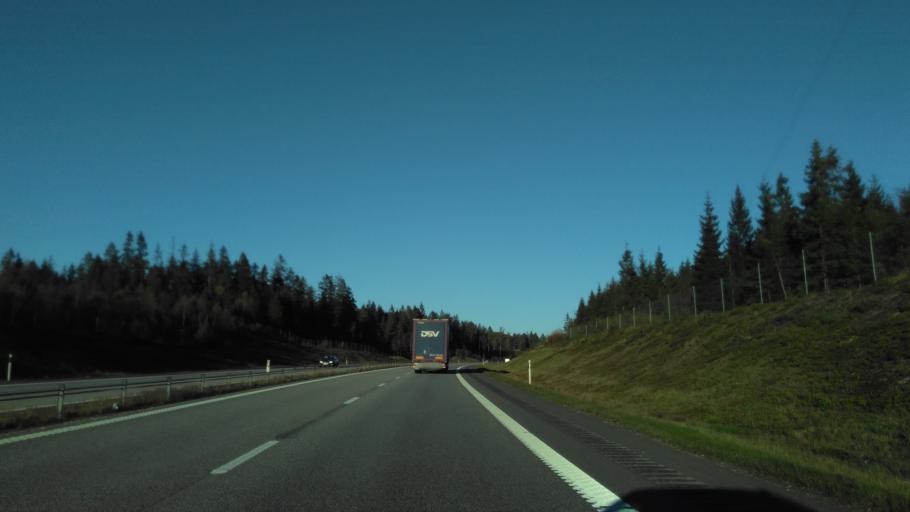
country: SE
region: Vaestra Goetaland
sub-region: Boras Kommun
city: Ganghester
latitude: 57.7369
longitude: 13.0427
